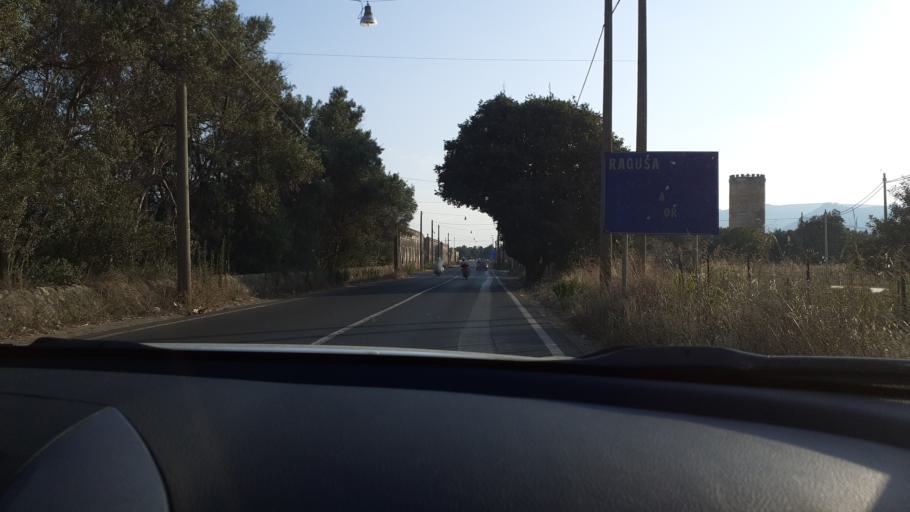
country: IT
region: Sicily
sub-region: Provincia di Siracusa
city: Cassibile
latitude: 36.9741
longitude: 15.1945
